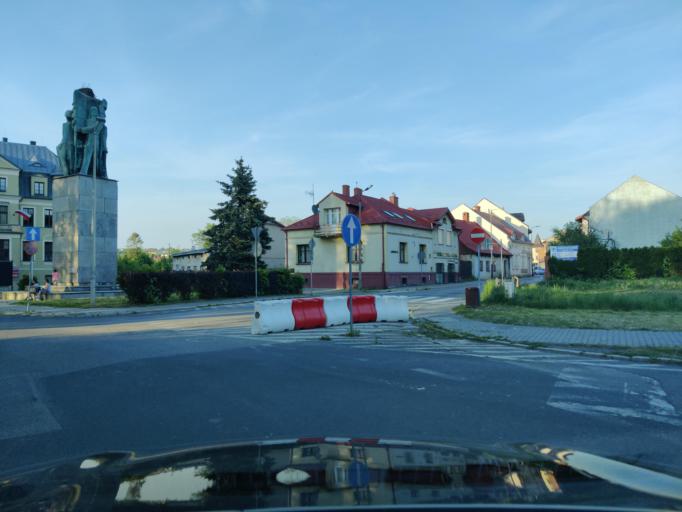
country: PL
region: Silesian Voivodeship
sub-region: Powiat zywiecki
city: Zywiec
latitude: 49.6882
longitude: 19.1946
